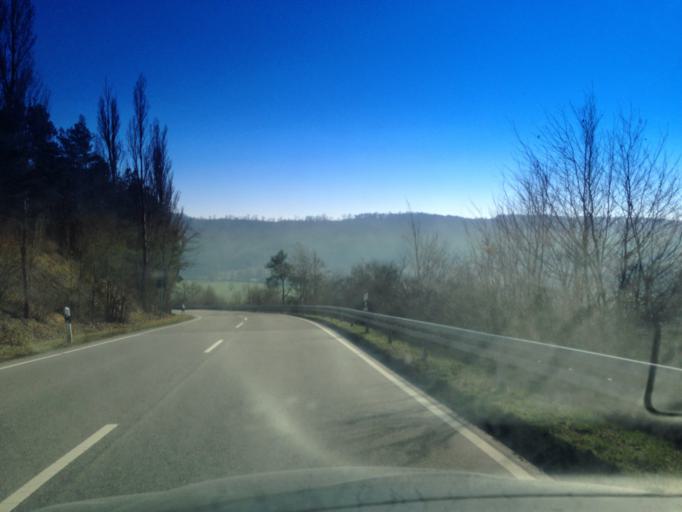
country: DE
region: Baden-Wuerttemberg
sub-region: Karlsruhe Region
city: Illingen
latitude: 48.9381
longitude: 8.9077
